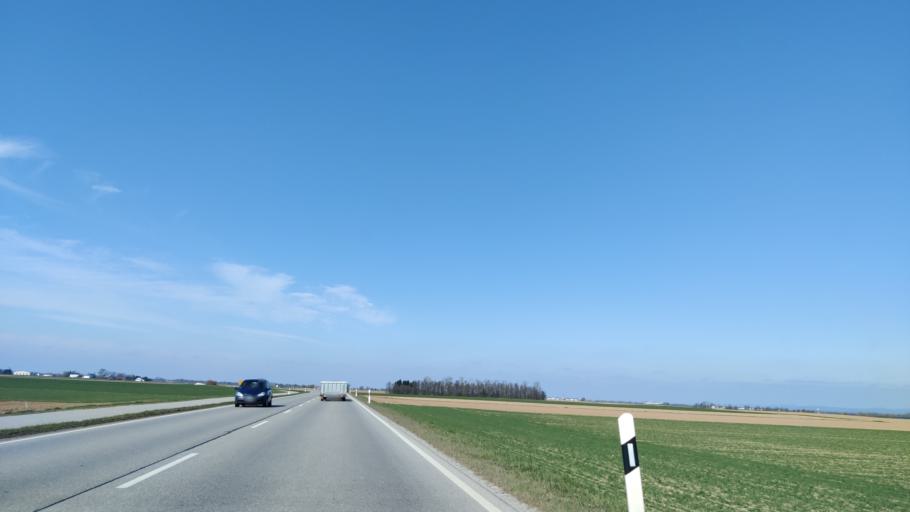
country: DE
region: Bavaria
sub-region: Lower Bavaria
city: Strasskirchen
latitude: 48.8388
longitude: 12.6951
